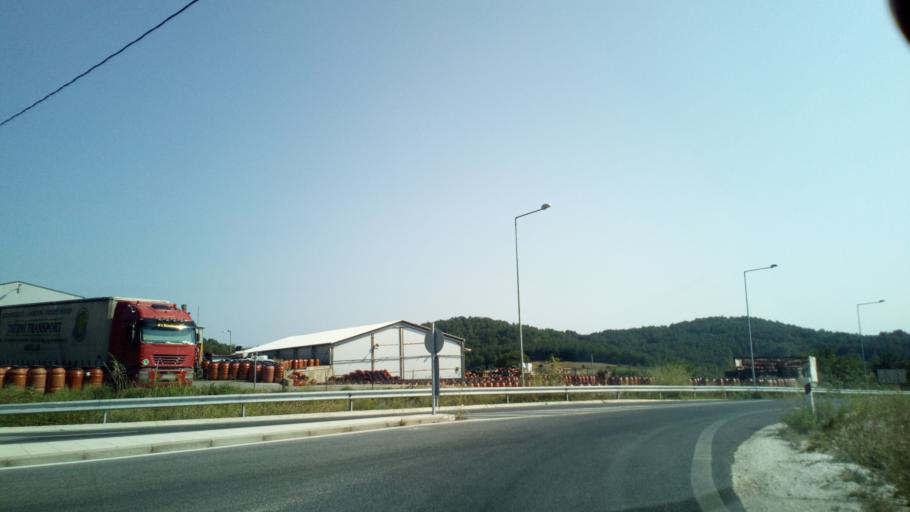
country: GR
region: Central Macedonia
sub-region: Nomos Chalkidikis
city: Polygyros
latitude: 40.3739
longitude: 23.4537
